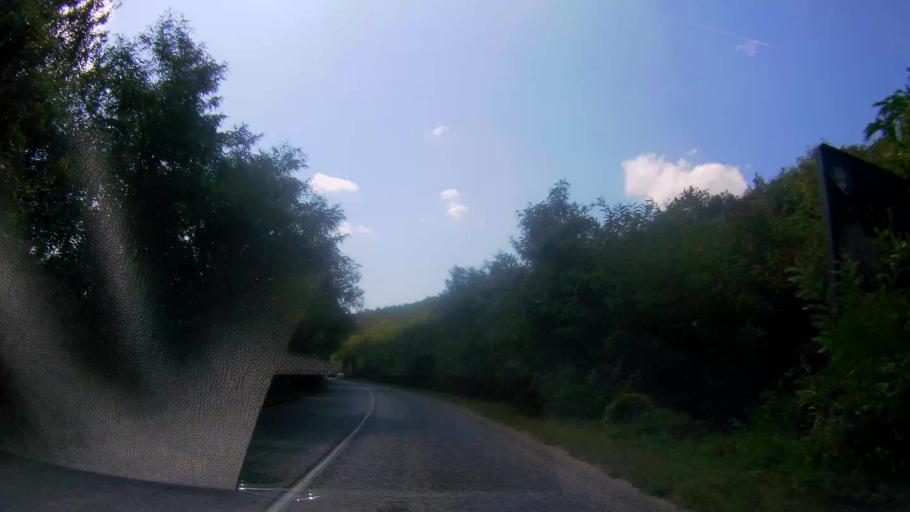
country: BG
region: Veliko Turnovo
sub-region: Obshtina Polski Trumbesh
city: Polski Trumbesh
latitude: 43.4395
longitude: 25.6542
